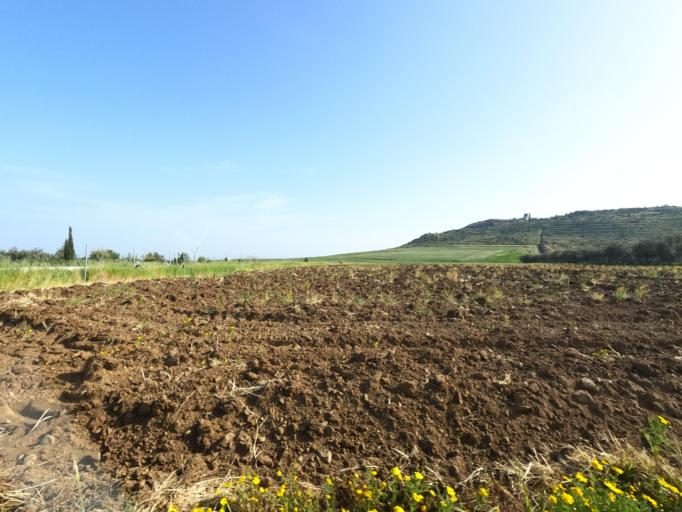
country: CY
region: Lefkosia
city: Lefka
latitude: 35.0887
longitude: 32.9493
